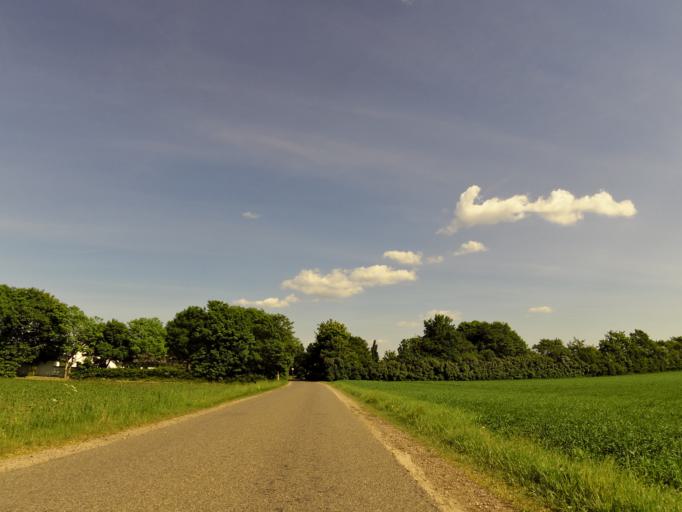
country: DK
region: Central Jutland
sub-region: Holstebro Kommune
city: Vinderup
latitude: 56.4333
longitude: 8.8890
